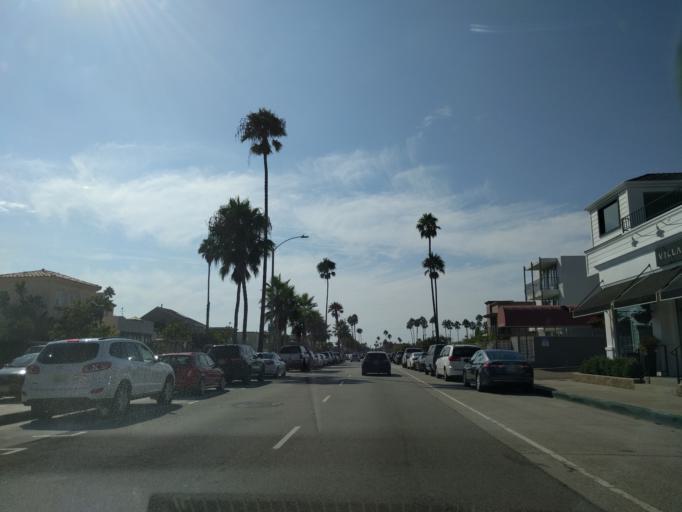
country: US
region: California
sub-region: Orange County
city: Newport Beach
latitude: 33.6072
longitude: -117.9209
